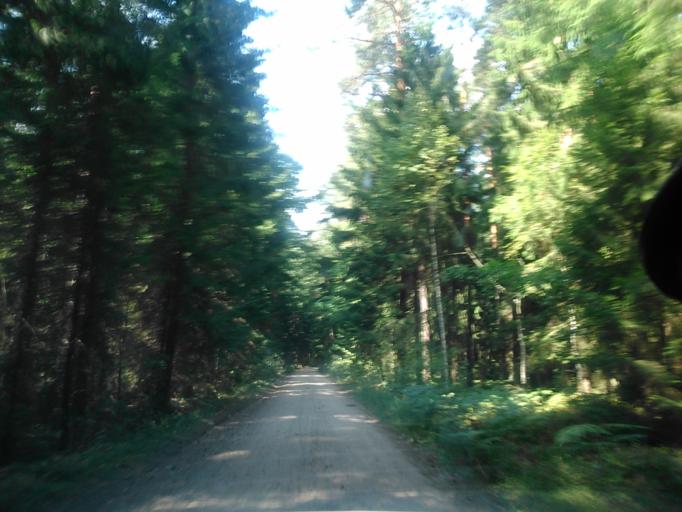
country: PL
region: Masovian Voivodeship
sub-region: Powiat ostrolecki
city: Czarnia
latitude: 53.3354
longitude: 21.2003
